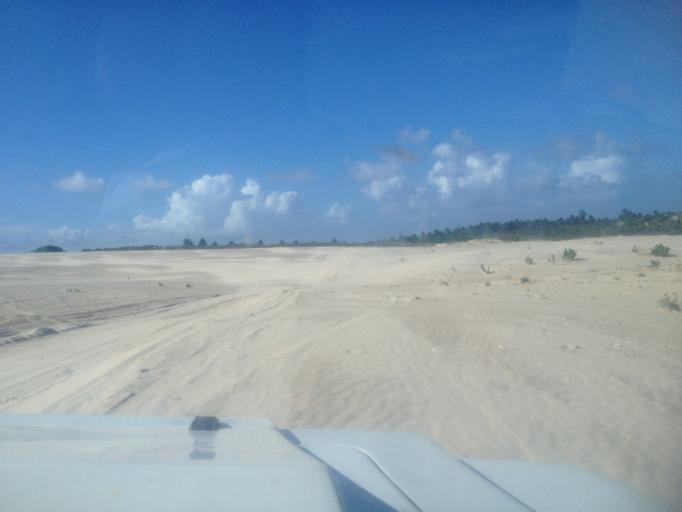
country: BR
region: Sergipe
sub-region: Indiaroba
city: Indiaroba
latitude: -11.4675
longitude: -37.3665
